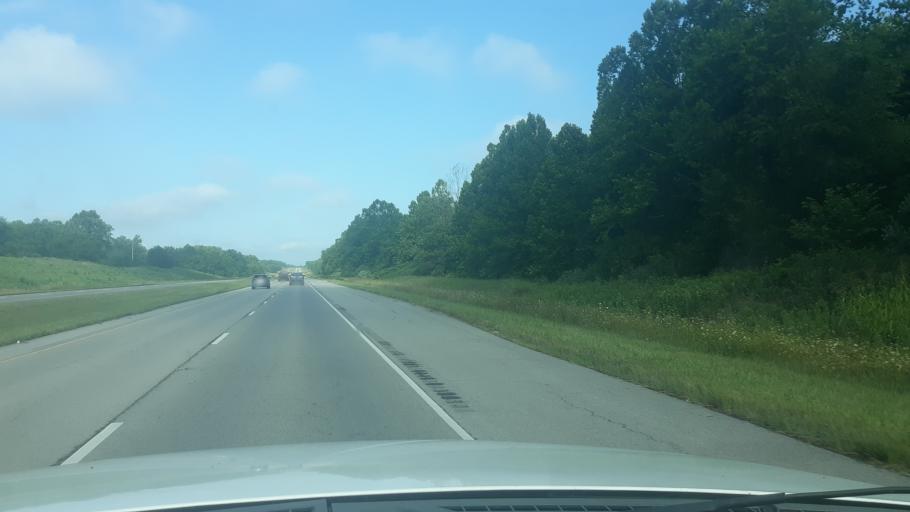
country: US
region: Illinois
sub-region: Saline County
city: Carrier Mills
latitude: 37.7308
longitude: -88.7437
